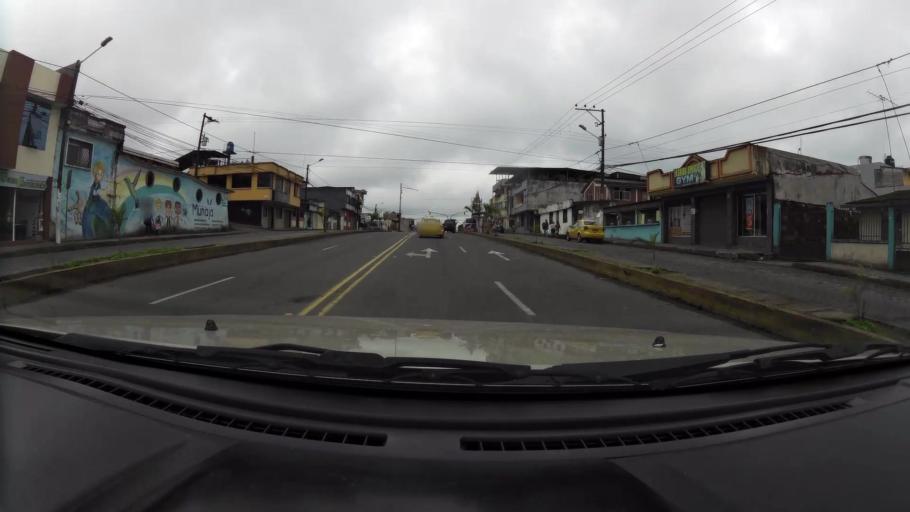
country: EC
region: Santo Domingo de los Tsachilas
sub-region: Canton Santo Domingo de los Colorados
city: Santo Domingo de los Colorados
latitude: -0.2482
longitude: -79.1837
